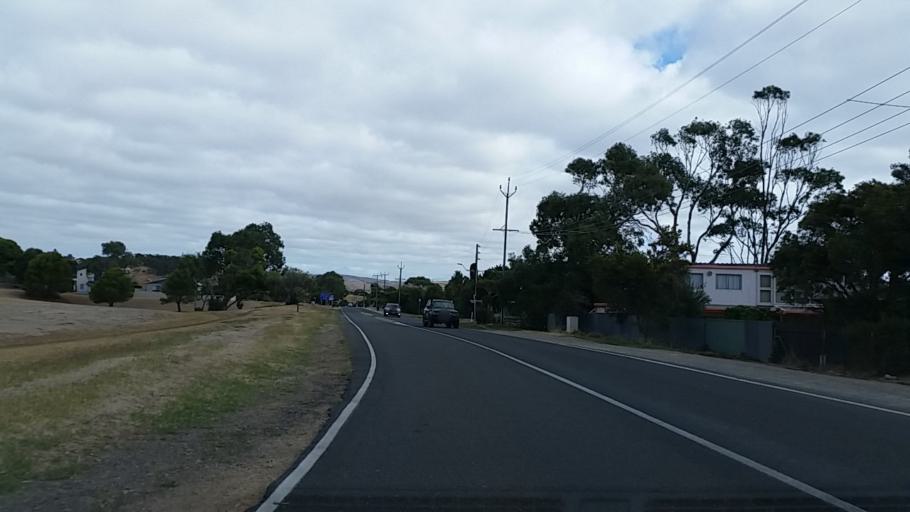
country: AU
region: South Australia
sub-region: Yankalilla
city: Normanville
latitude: -35.4263
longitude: 138.3276
